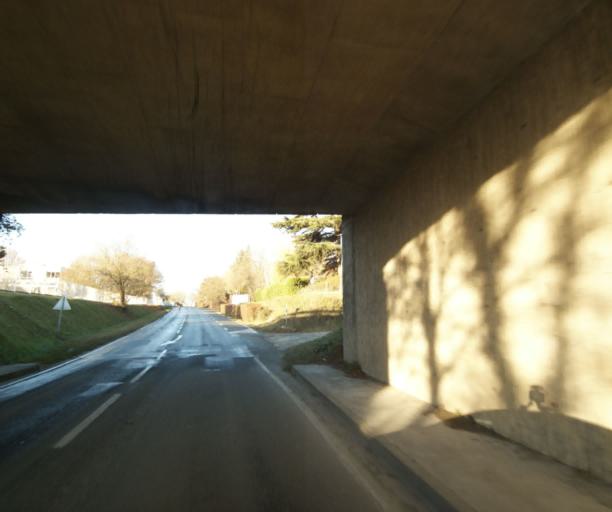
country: FR
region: Poitou-Charentes
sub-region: Departement de la Charente-Maritime
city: Saintes
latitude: 45.7493
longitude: -0.6612
